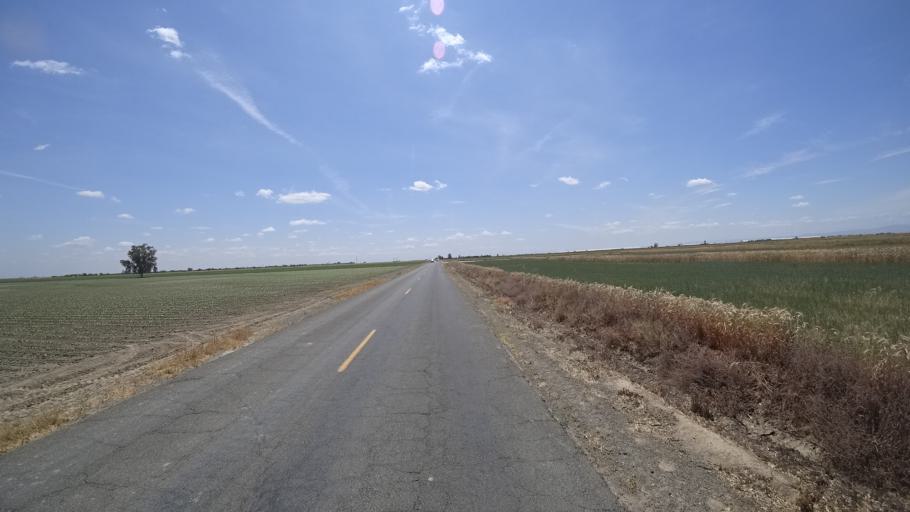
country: US
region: California
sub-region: Kings County
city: Home Garden
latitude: 36.2201
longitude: -119.6728
